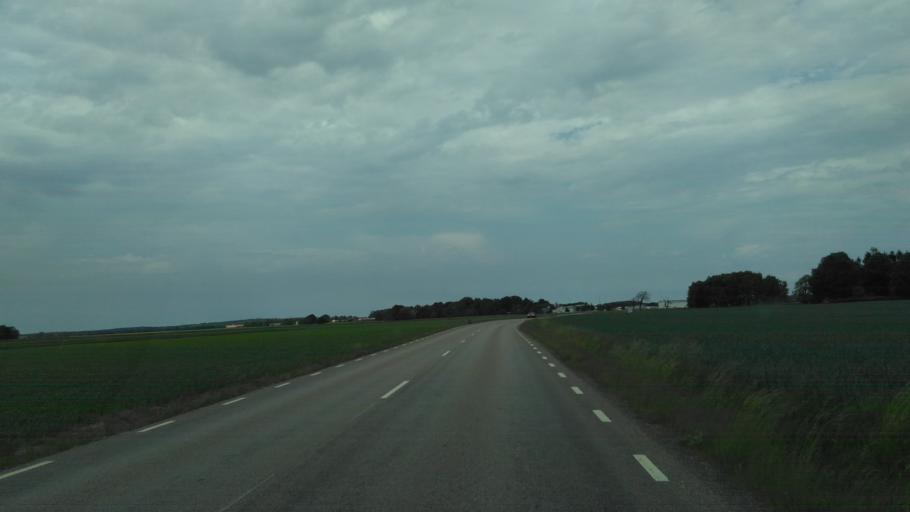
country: SE
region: Vaestra Goetaland
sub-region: Lidkopings Kommun
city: Lidkoping
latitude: 58.4536
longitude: 13.1580
